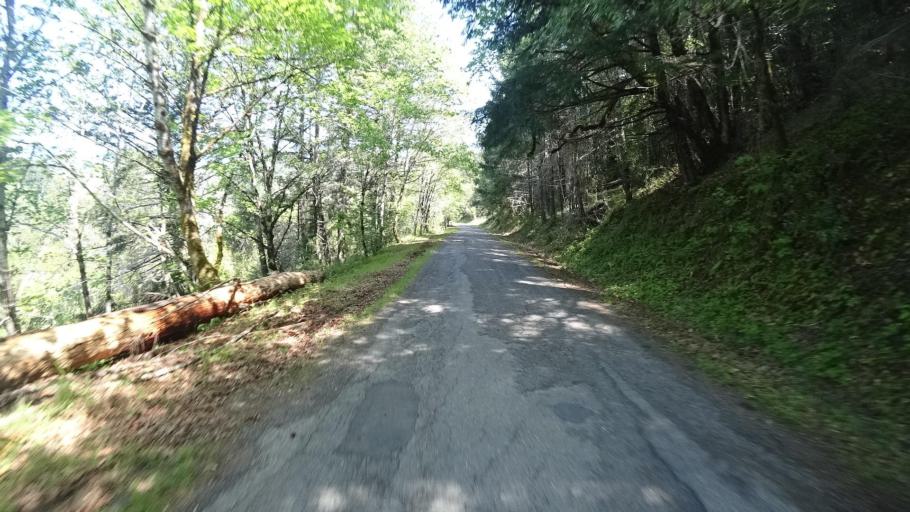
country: US
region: California
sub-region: Humboldt County
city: Redway
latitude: 40.2327
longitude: -123.6416
